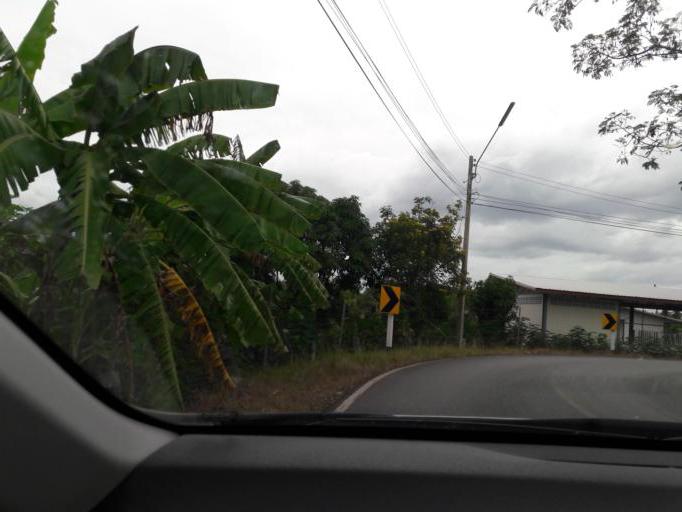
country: TH
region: Ratchaburi
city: Damnoen Saduak
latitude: 13.5443
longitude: 100.0058
